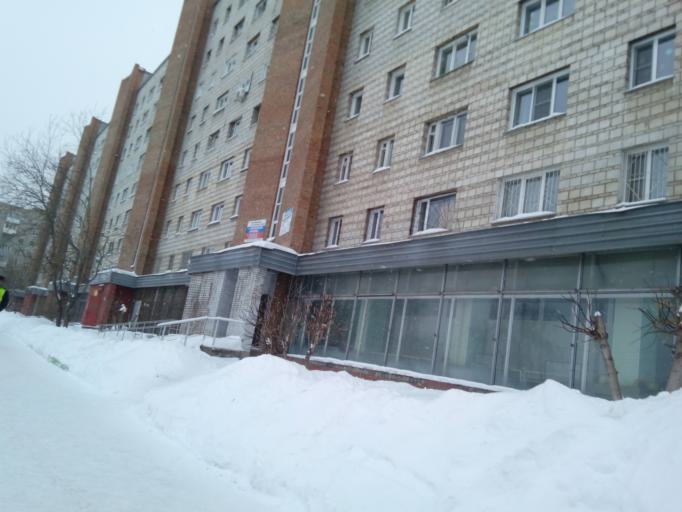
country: RU
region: Novosibirsk
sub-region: Novosibirskiy Rayon
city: Novosibirsk
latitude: 54.9940
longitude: 82.8623
